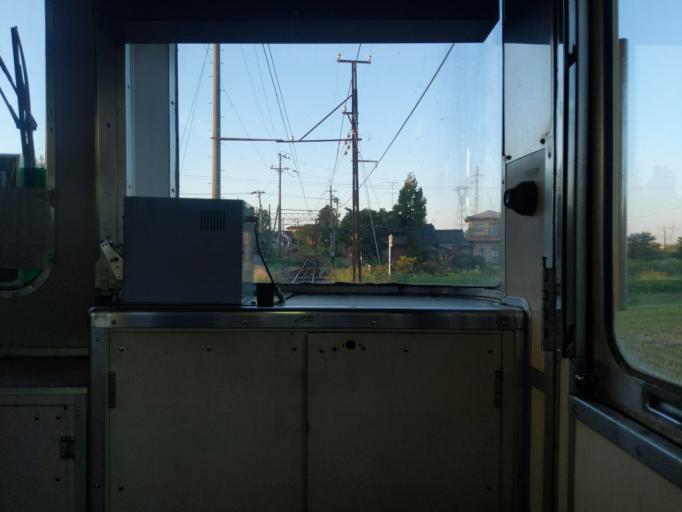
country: JP
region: Toyama
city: Kamiichi
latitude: 36.6970
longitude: 137.3187
